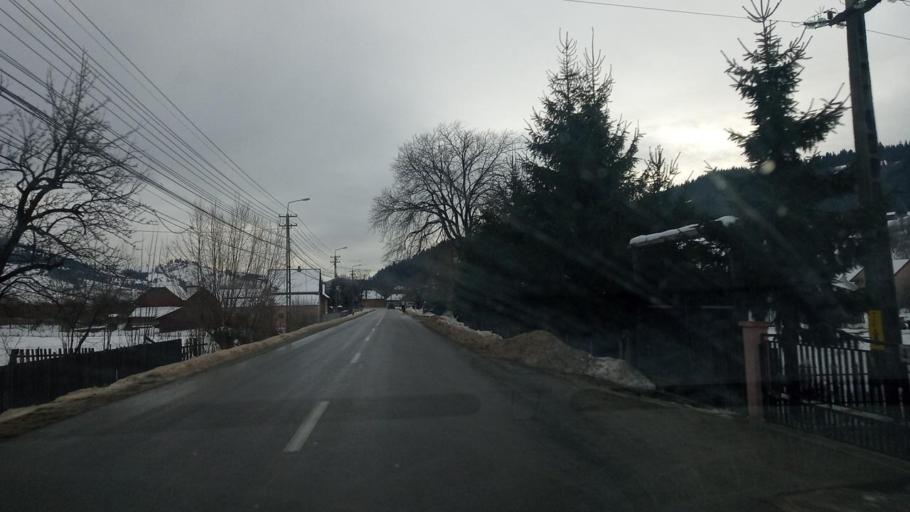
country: RO
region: Suceava
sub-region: Comuna Frasin
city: Frasin
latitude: 47.5237
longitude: 25.7978
